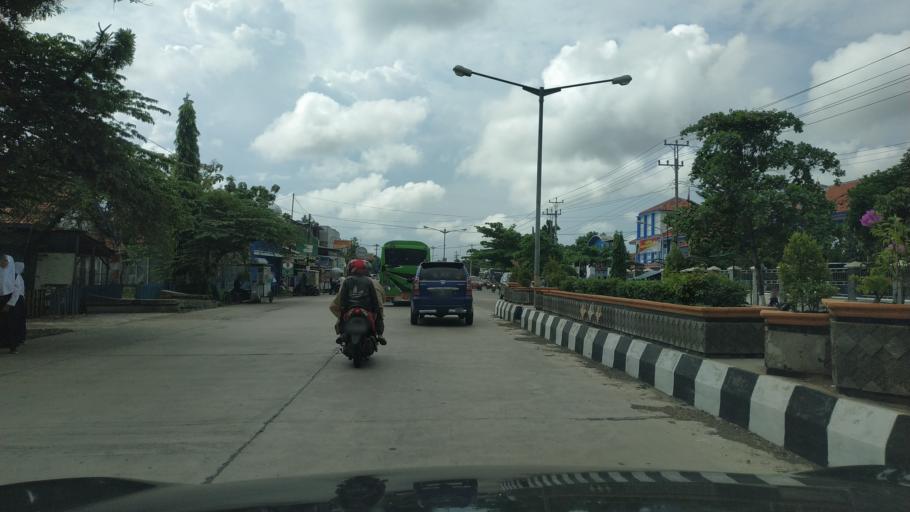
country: ID
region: Central Java
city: Pemalang
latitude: -6.9071
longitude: 109.3830
